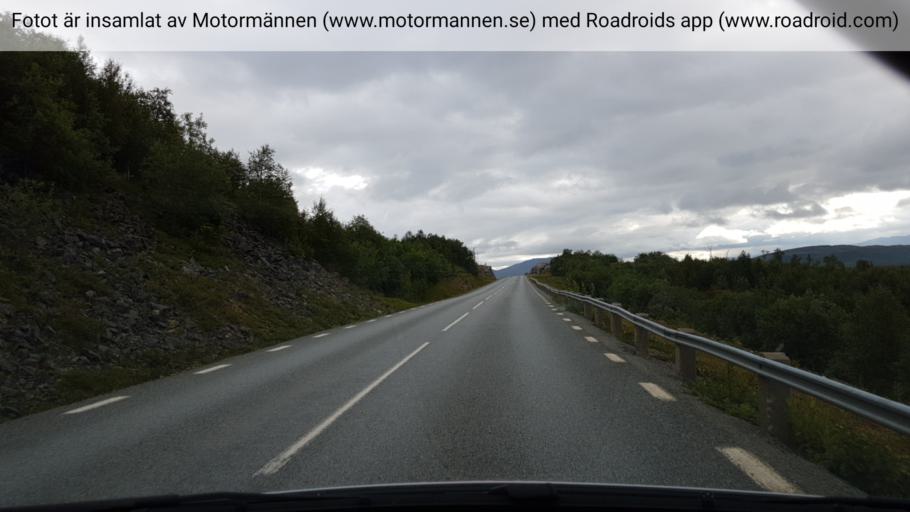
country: NO
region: Nordland
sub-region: Rana
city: Mo i Rana
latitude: 66.1233
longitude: 14.6795
